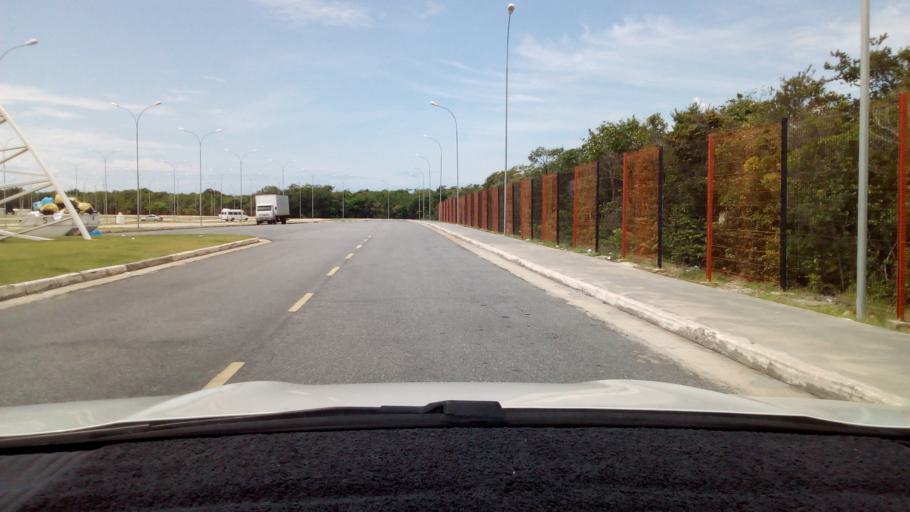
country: BR
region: Paraiba
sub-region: Joao Pessoa
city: Joao Pessoa
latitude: -7.1881
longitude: -34.8058
